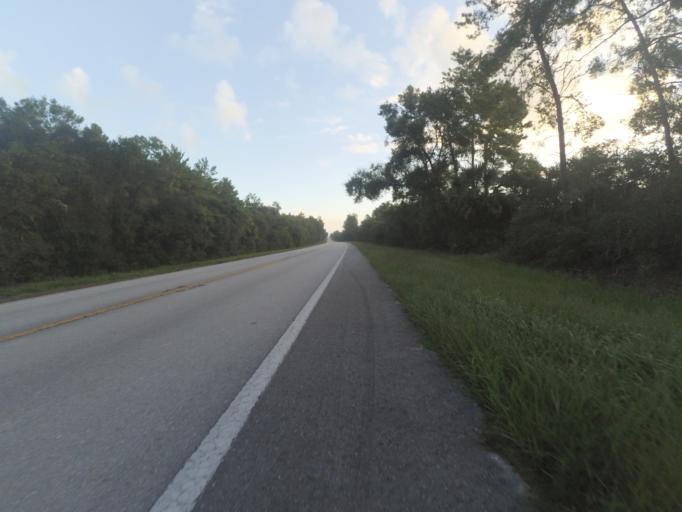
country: US
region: Florida
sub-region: Lake County
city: Astor
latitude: 29.2506
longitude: -81.6464
